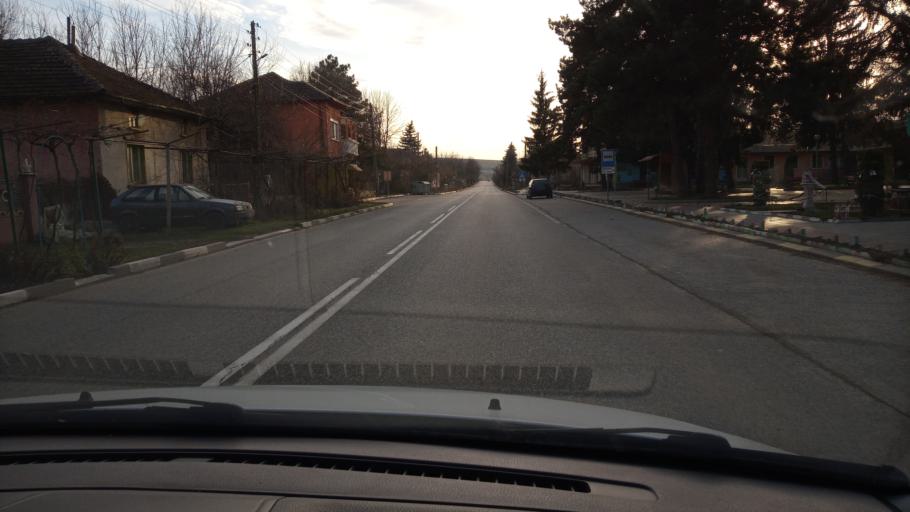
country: BG
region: Pleven
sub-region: Obshtina Pleven
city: Slavyanovo
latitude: 43.5539
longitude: 24.8652
